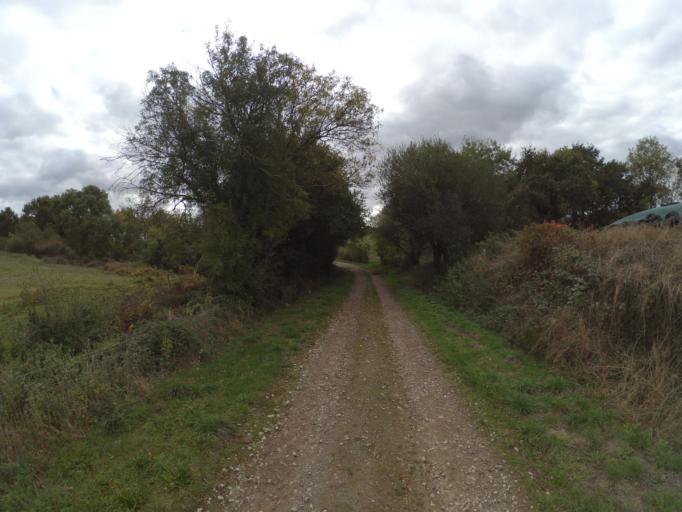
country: FR
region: Pays de la Loire
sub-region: Departement de la Loire-Atlantique
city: Remouille
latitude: 47.0529
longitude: -1.3567
